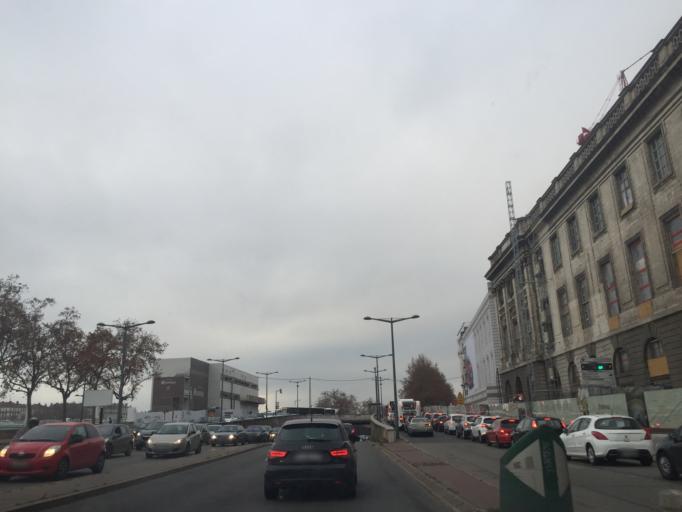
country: FR
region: Rhone-Alpes
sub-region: Departement du Rhone
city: Lyon
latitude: 45.7588
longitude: 4.8373
